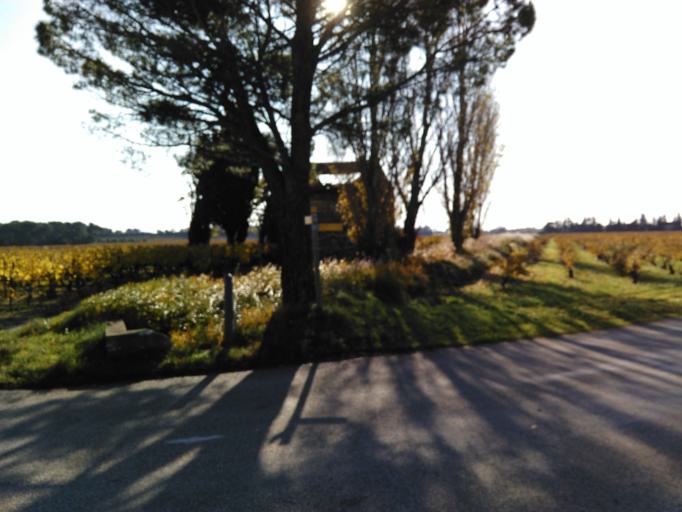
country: FR
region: Provence-Alpes-Cote d'Azur
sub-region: Departement du Vaucluse
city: Sainte-Cecile-les-Vignes
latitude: 44.2386
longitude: 4.8734
